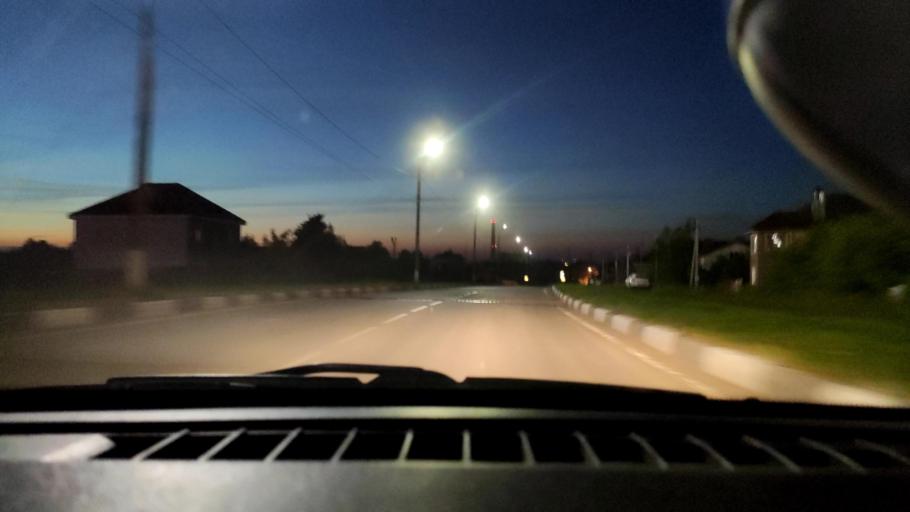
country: RU
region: Samara
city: Novokuybyshevsk
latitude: 53.0899
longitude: 49.9967
